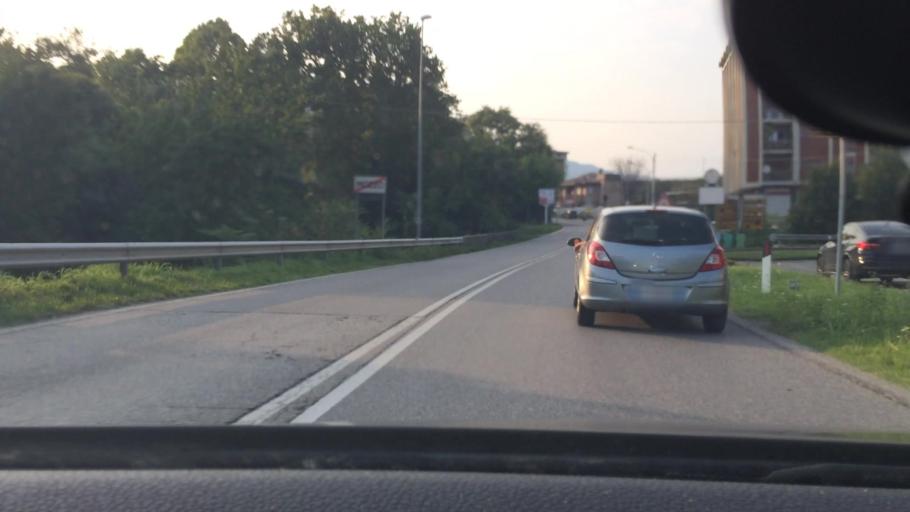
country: IT
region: Lombardy
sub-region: Provincia di Bergamo
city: Ponte San Pietro
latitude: 45.6979
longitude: 9.5950
